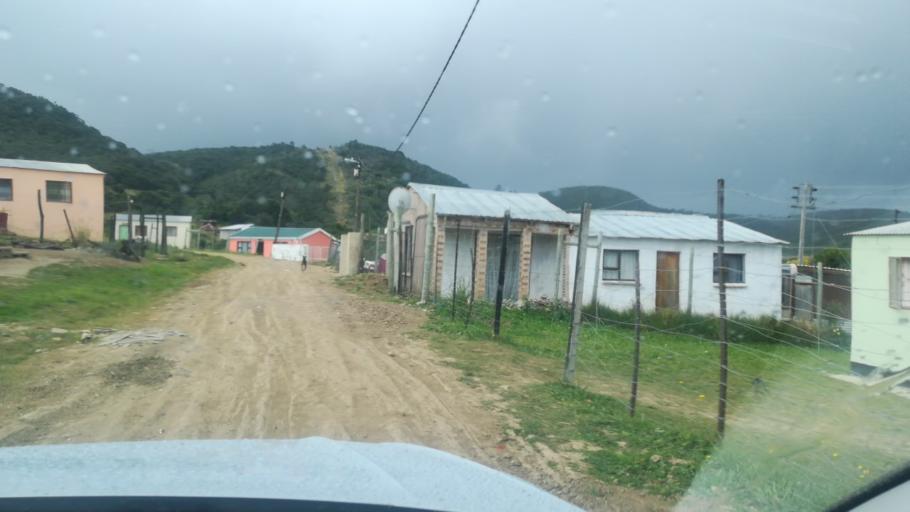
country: ZA
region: Eastern Cape
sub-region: Buffalo City Metropolitan Municipality
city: East London
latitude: -32.9951
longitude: 27.7988
